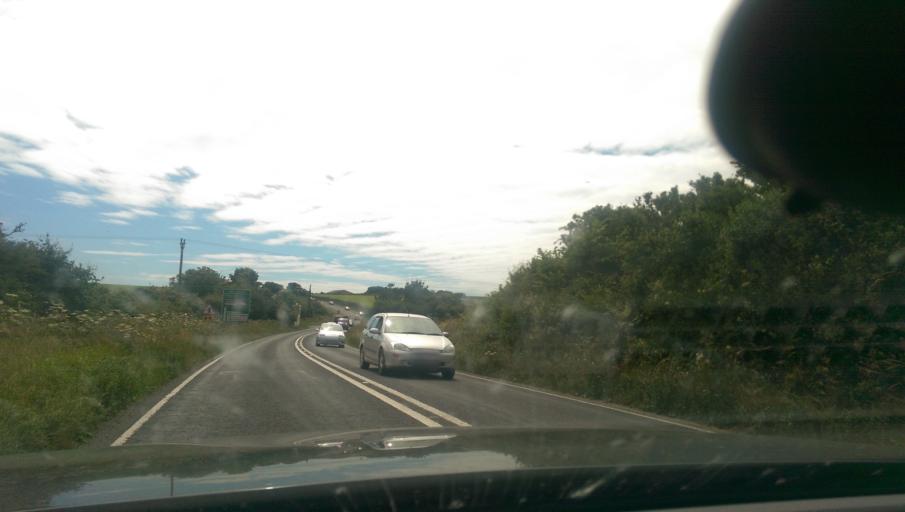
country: GB
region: England
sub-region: Cornwall
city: Wadebridge
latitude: 50.5092
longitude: -4.8794
